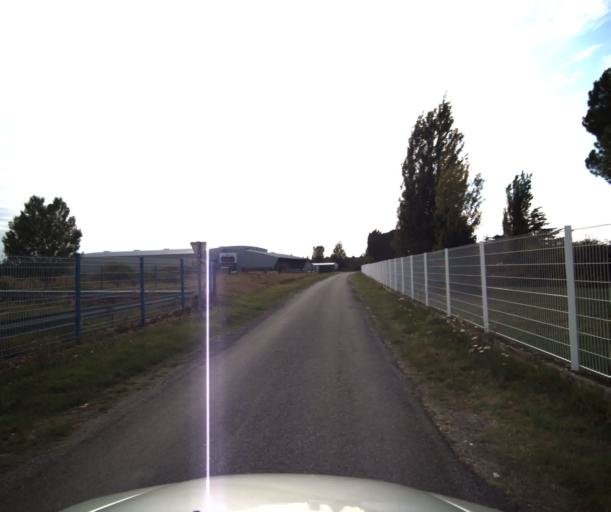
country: FR
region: Midi-Pyrenees
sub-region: Departement de la Haute-Garonne
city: Muret
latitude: 43.4411
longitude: 1.3129
